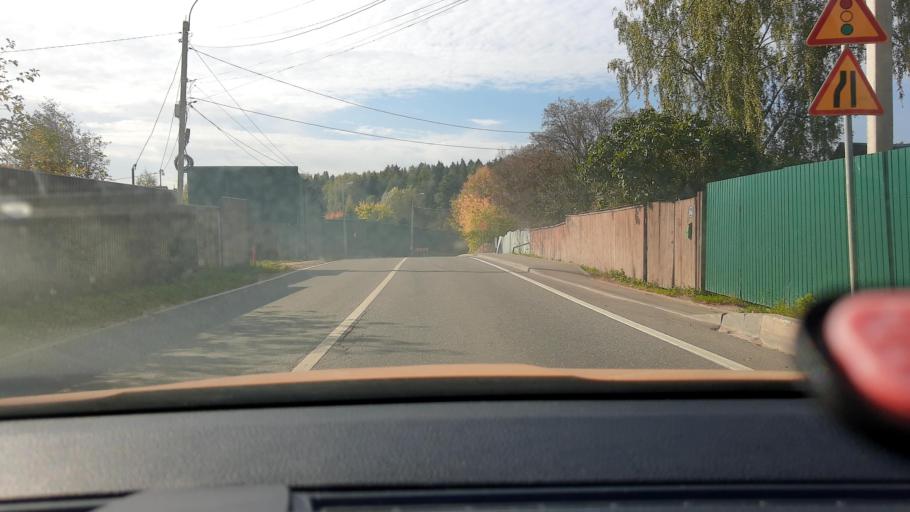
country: RU
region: Moskovskaya
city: Opalikha
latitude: 55.7891
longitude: 37.2166
